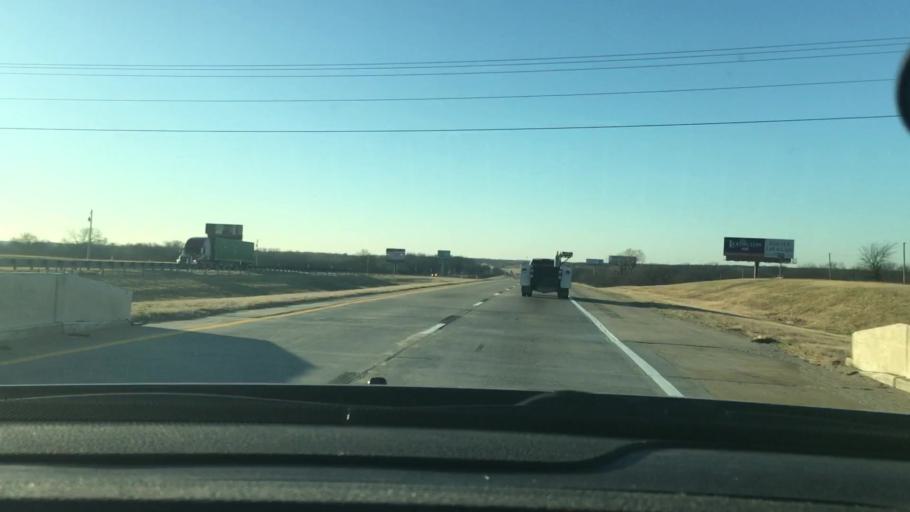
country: US
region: Oklahoma
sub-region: Carter County
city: Ardmore
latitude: 34.2751
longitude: -97.1620
